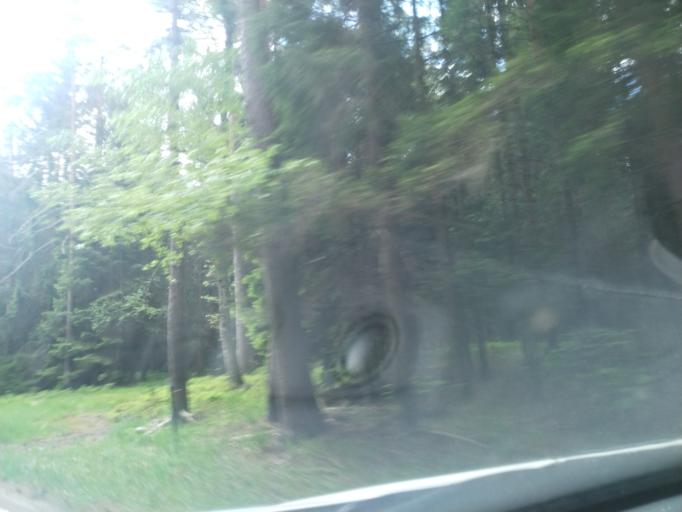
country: DE
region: Baden-Wuerttemberg
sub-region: Karlsruhe Region
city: Baiersbronn
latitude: 48.5710
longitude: 8.4253
